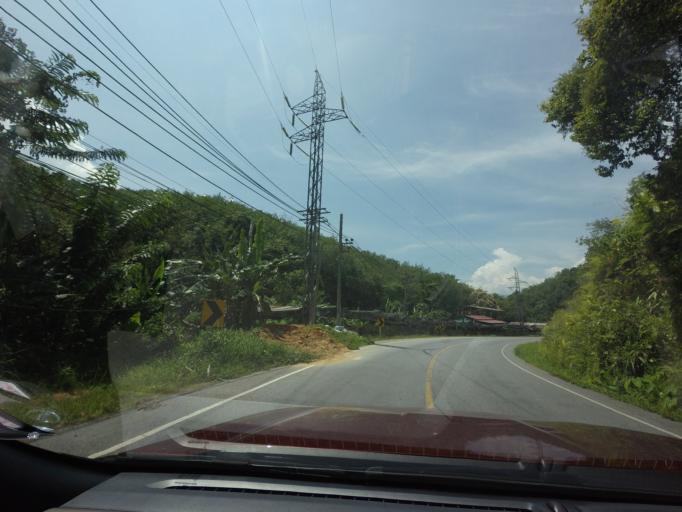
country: TH
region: Yala
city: Betong
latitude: 5.9187
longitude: 101.1581
